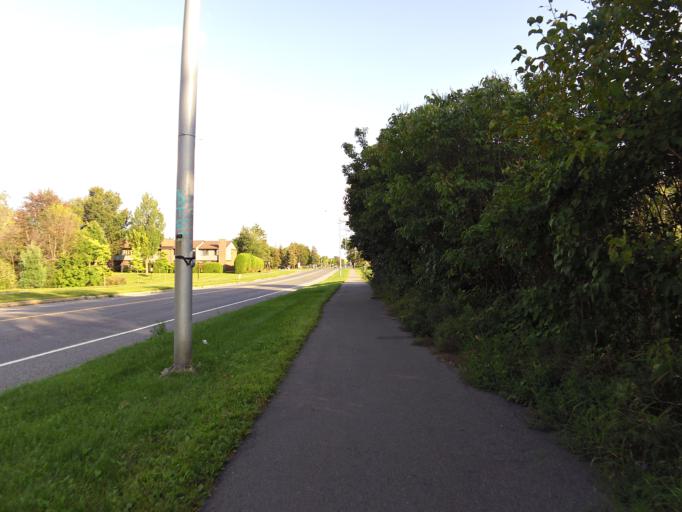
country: CA
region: Ontario
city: Bells Corners
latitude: 45.3315
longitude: -75.9025
